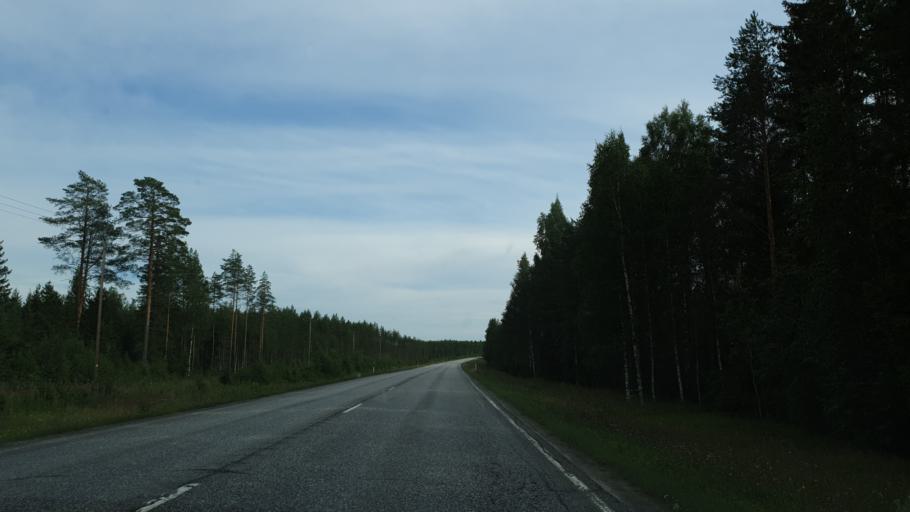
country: FI
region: North Karelia
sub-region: Joensuu
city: Kontiolahti
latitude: 62.9710
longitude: 29.7852
